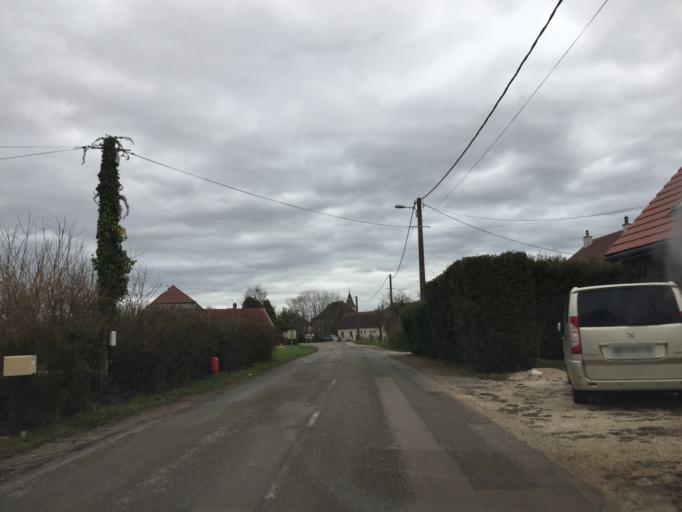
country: FR
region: Franche-Comte
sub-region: Departement du Doubs
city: Arc-et-Senans
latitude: 47.0218
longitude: 5.7154
